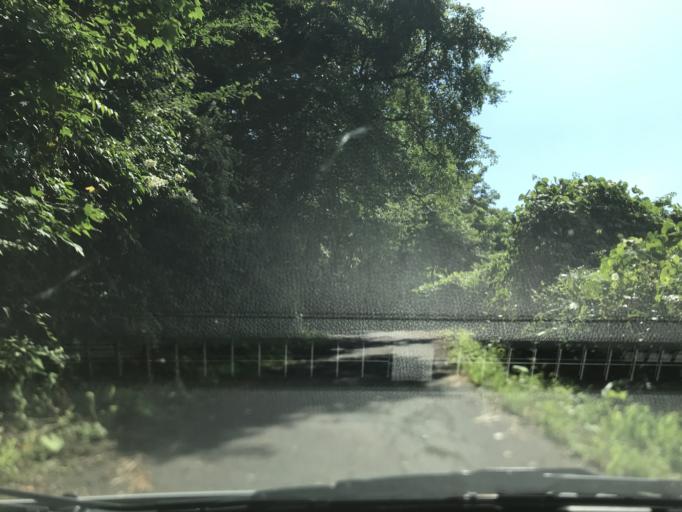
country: JP
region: Iwate
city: Ofunato
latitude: 38.9878
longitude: 141.4288
